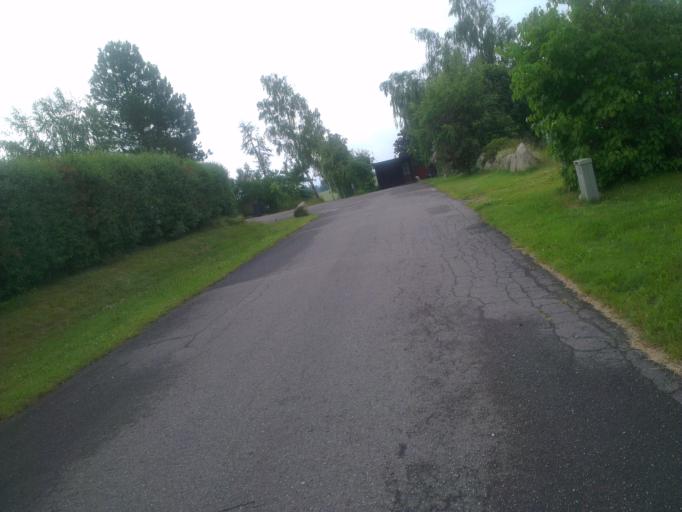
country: DK
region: Capital Region
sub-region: Frederikssund Kommune
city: Jaegerspris
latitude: 55.9133
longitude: 11.9263
